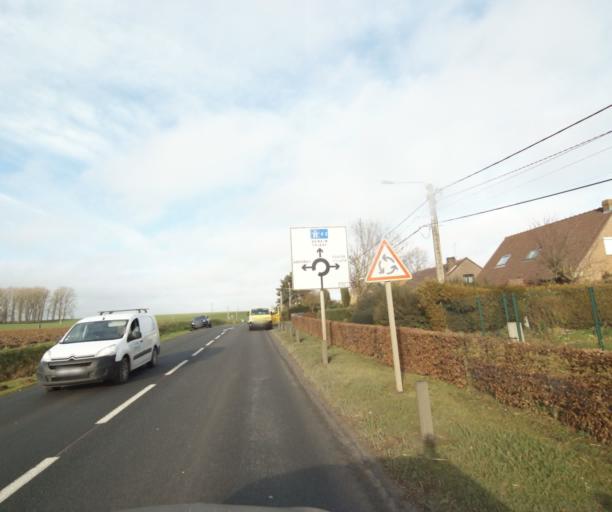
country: FR
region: Nord-Pas-de-Calais
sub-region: Departement du Nord
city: Thiant
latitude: 50.2840
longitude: 3.4503
